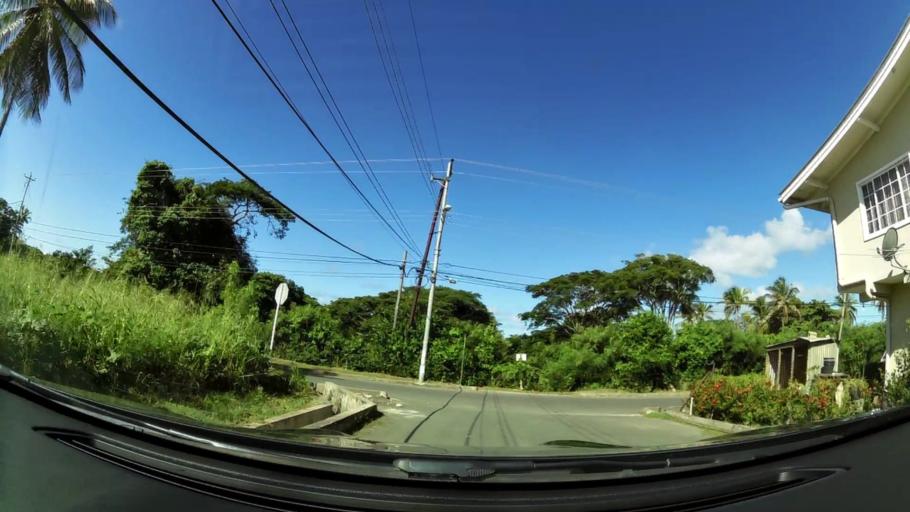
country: TT
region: Tobago
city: Scarborough
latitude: 11.1560
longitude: -60.7880
